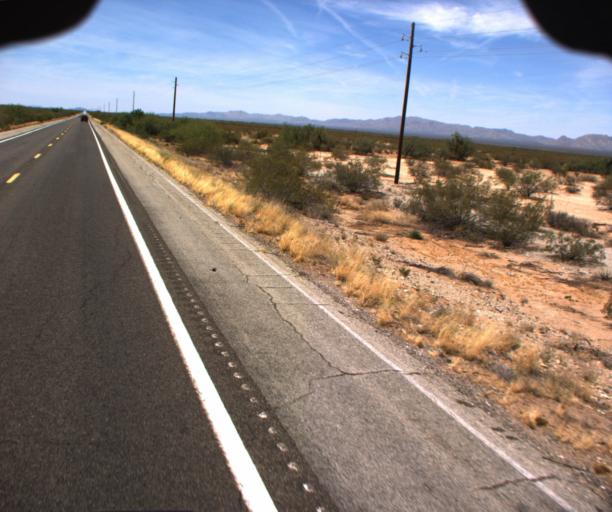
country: US
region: Arizona
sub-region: La Paz County
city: Salome
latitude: 33.8877
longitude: -113.3428
